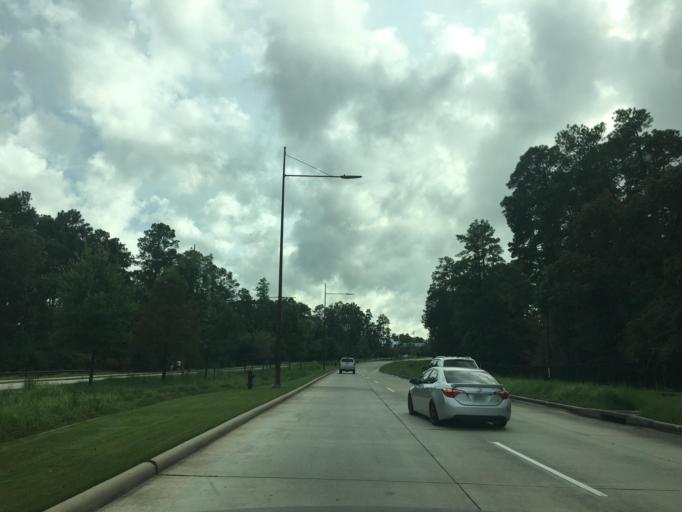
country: US
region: Texas
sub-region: Harris County
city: Spring
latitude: 30.1034
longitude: -95.4407
